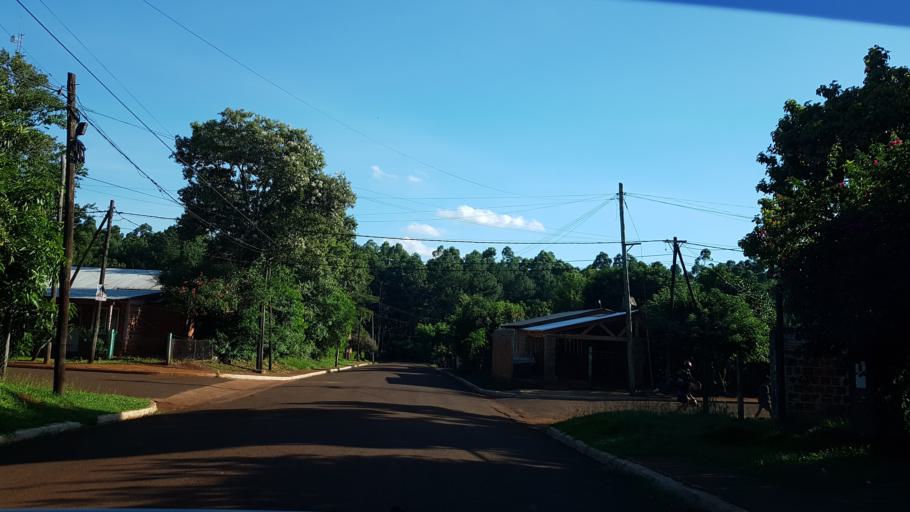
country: AR
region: Misiones
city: Puerto Libertad
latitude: -25.9234
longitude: -54.5882
